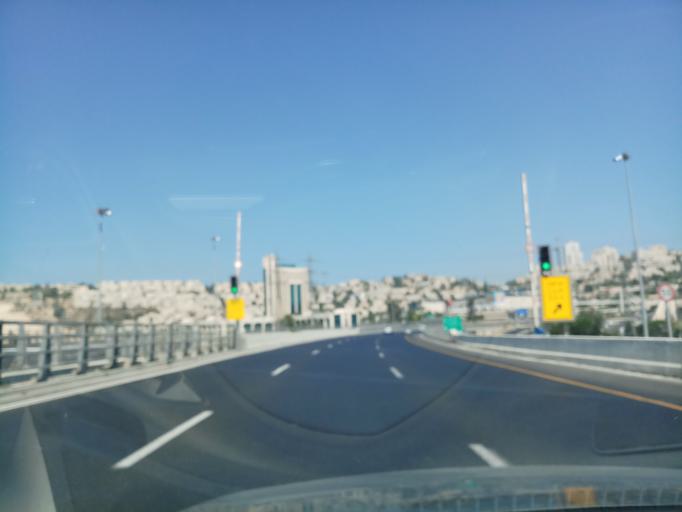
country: PS
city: Khallat Hamamah
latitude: 31.7477
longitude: 35.1912
